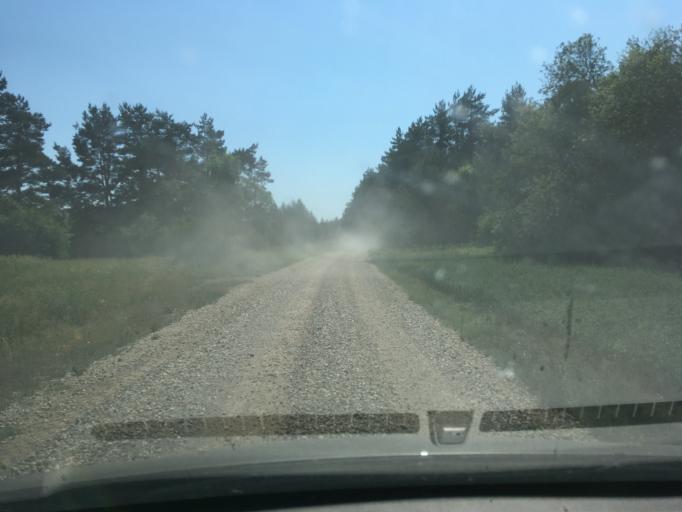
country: EE
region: Laeaene
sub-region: Lihula vald
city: Lihula
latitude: 58.5755
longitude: 23.6991
